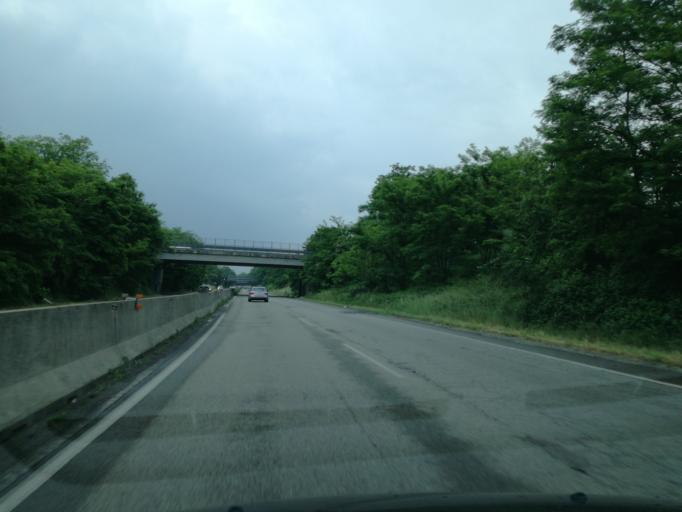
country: IT
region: Lombardy
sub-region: Provincia di Monza e Brianza
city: Villasanta
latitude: 45.5973
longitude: 9.3153
